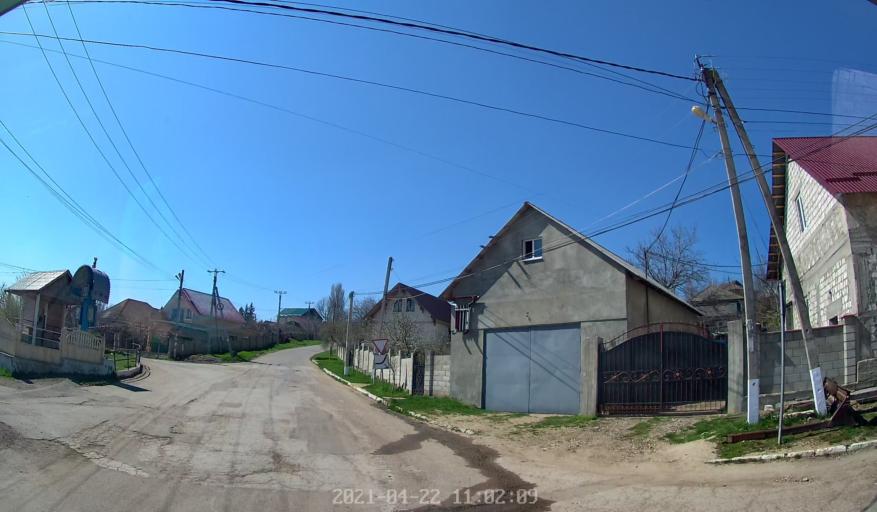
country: MD
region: Chisinau
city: Ciorescu
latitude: 47.1663
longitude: 28.9487
